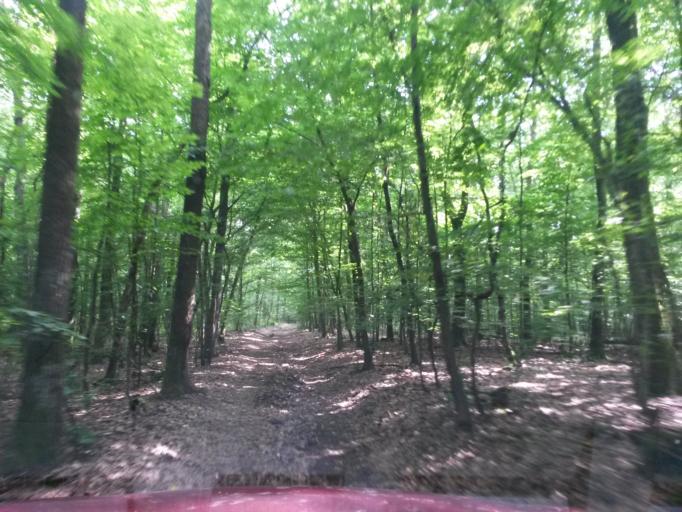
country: SK
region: Kosicky
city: Moldava nad Bodvou
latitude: 48.6255
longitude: 21.0995
